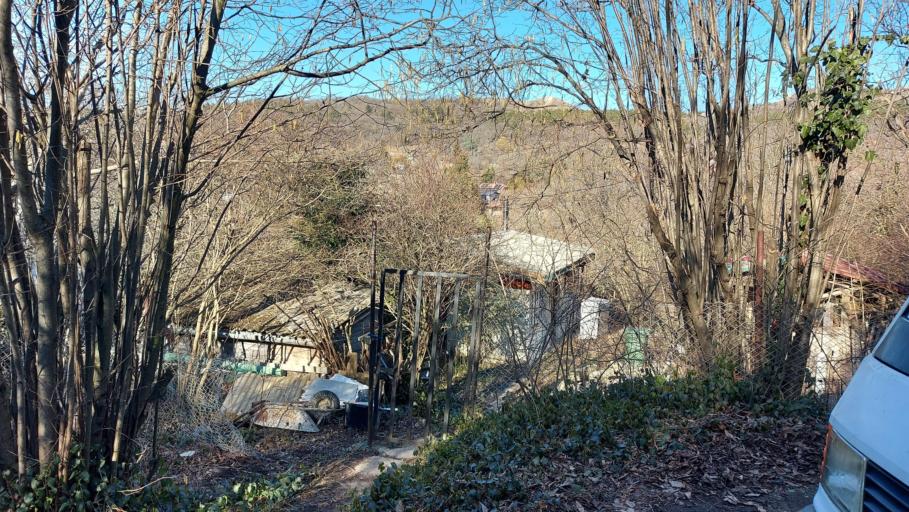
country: HU
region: Pest
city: Budaors
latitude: 47.4669
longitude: 18.9400
